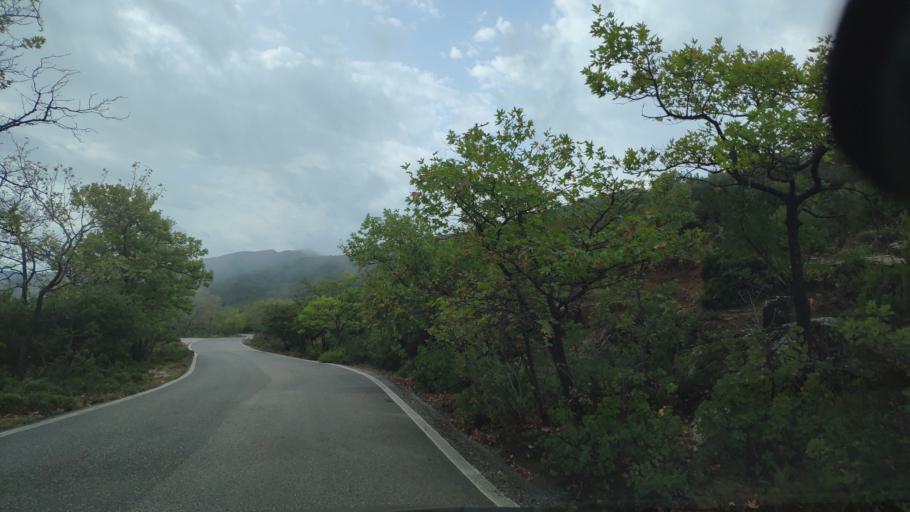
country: GR
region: West Greece
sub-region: Nomos Aitolias kai Akarnanias
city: Sardinia
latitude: 38.8464
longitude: 21.3168
